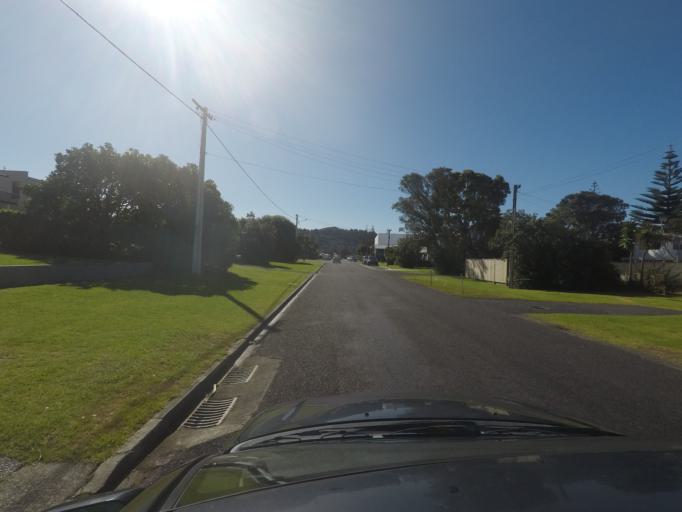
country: NZ
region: Bay of Plenty
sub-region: Western Bay of Plenty District
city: Waihi Beach
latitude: -37.4065
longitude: 175.9434
